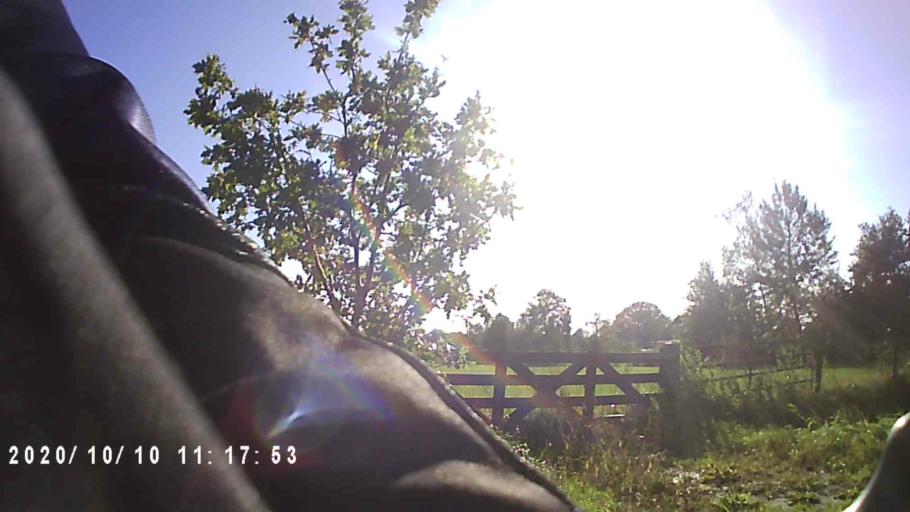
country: NL
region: Friesland
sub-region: Gemeente Smallingerland
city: Drachtstercompagnie
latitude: 53.0952
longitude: 6.1973
